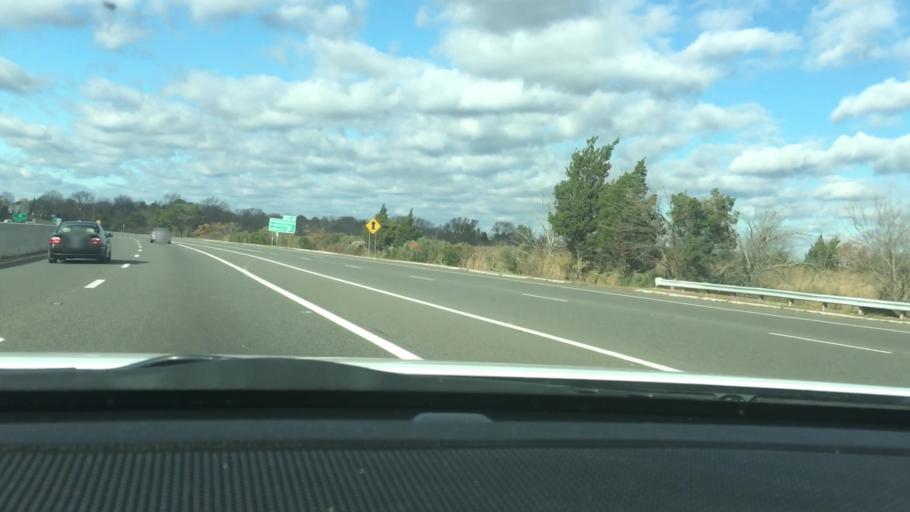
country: US
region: New Jersey
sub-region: Atlantic County
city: Pleasantville
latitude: 39.3931
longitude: -74.5109
